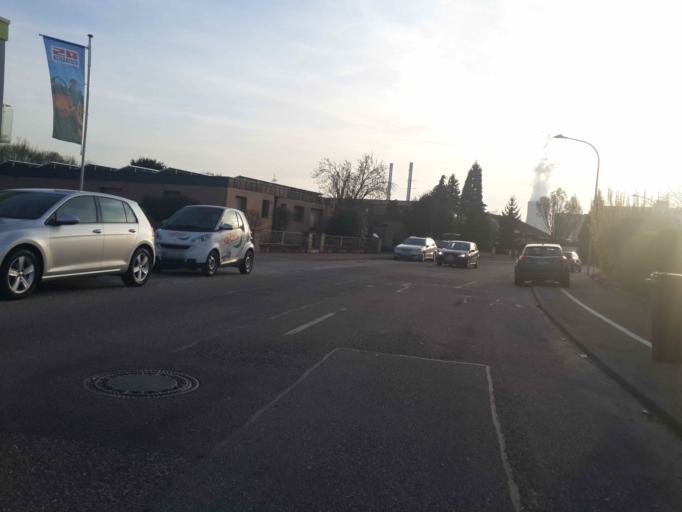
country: DE
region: Baden-Wuerttemberg
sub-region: Regierungsbezirk Stuttgart
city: Neckarsulm
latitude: 49.1837
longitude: 9.2326
